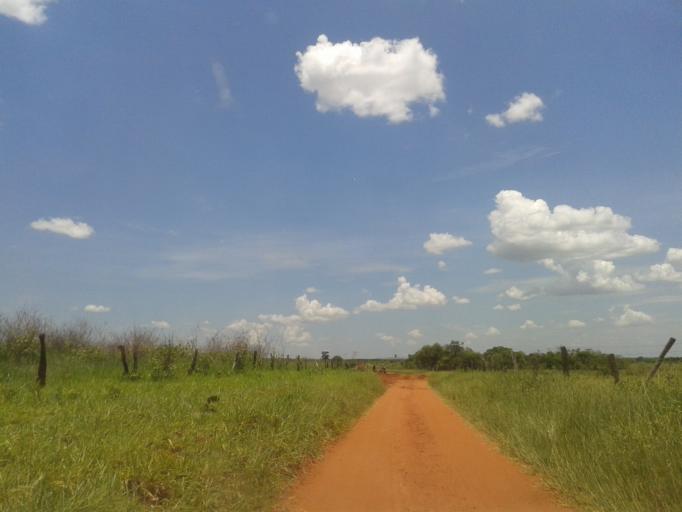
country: BR
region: Minas Gerais
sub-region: Santa Vitoria
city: Santa Vitoria
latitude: -19.2247
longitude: -50.4442
